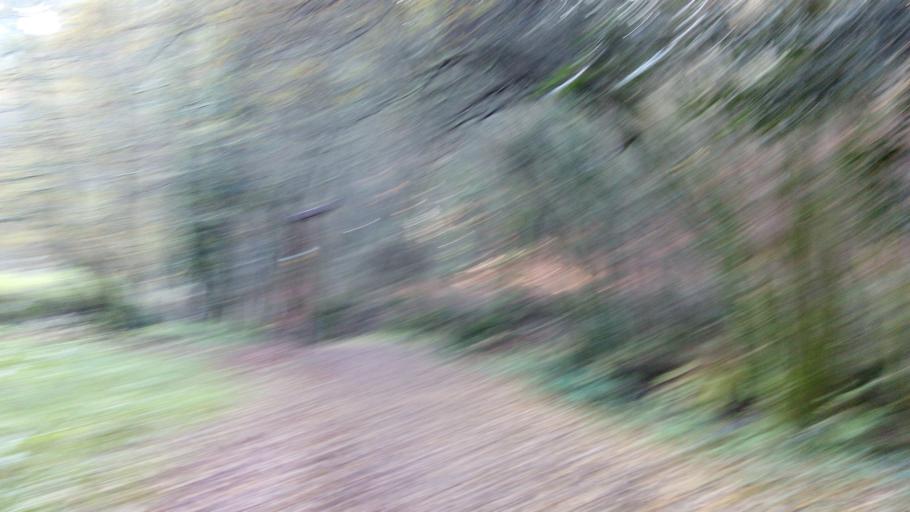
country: ES
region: Galicia
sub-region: Provincia de Pontevedra
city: Meis
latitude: 42.4868
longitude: -8.7501
